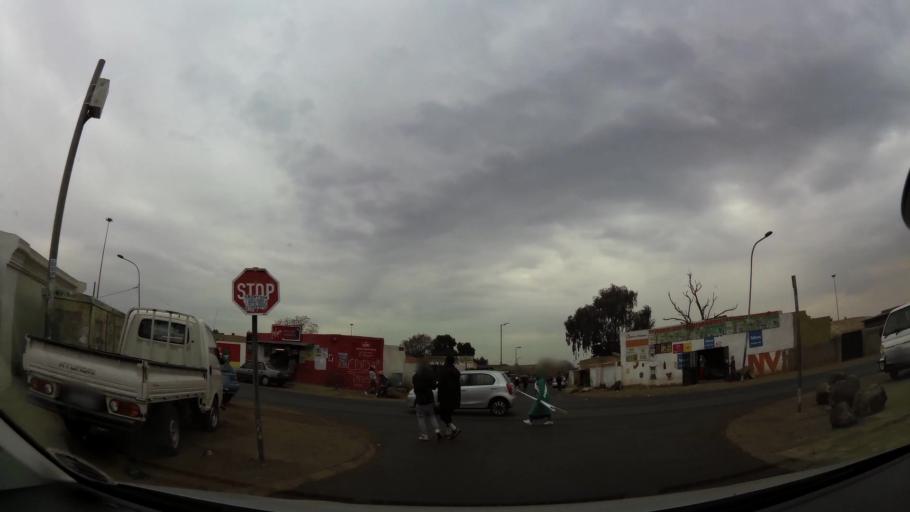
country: ZA
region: Gauteng
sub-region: City of Johannesburg Metropolitan Municipality
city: Soweto
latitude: -26.2533
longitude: 27.8761
